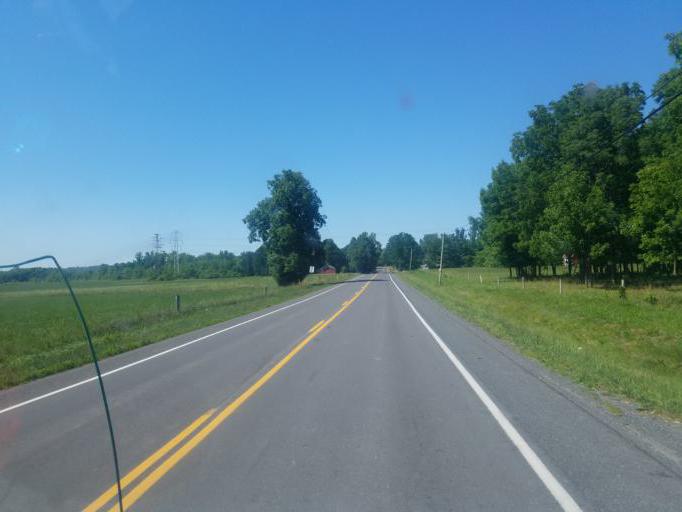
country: US
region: New York
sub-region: Ontario County
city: Phelps
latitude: 42.9425
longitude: -77.0131
